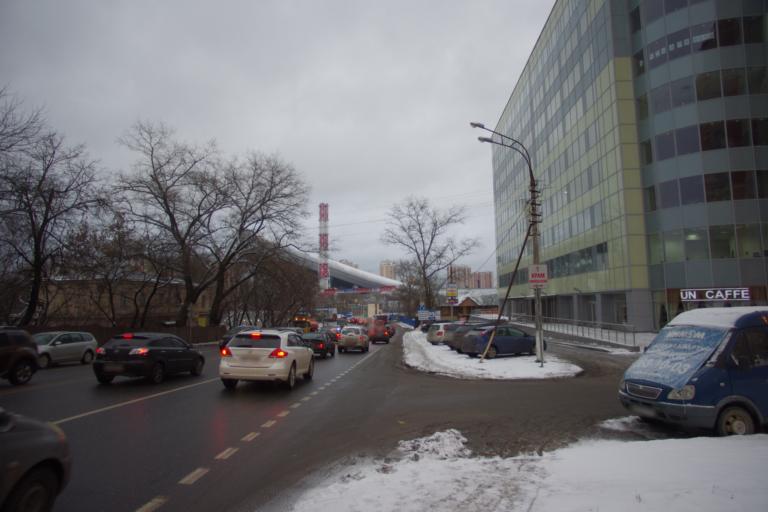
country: RU
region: Moskovskaya
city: Pavshino
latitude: 55.8156
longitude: 37.3522
